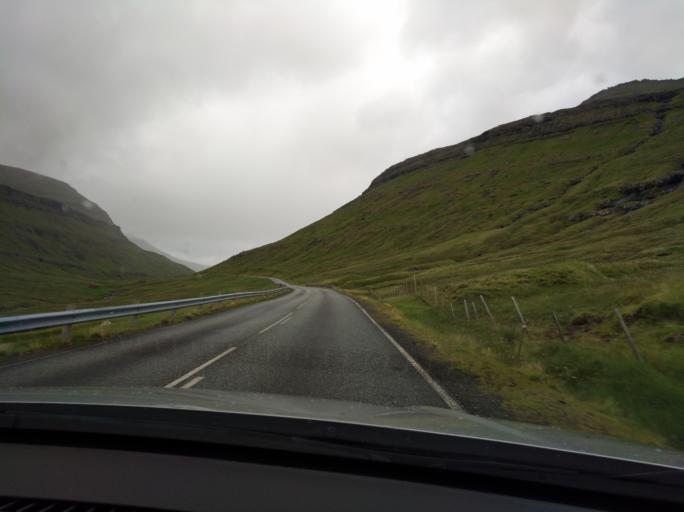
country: FO
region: Eysturoy
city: Fuglafjordur
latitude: 62.2258
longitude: -6.8796
